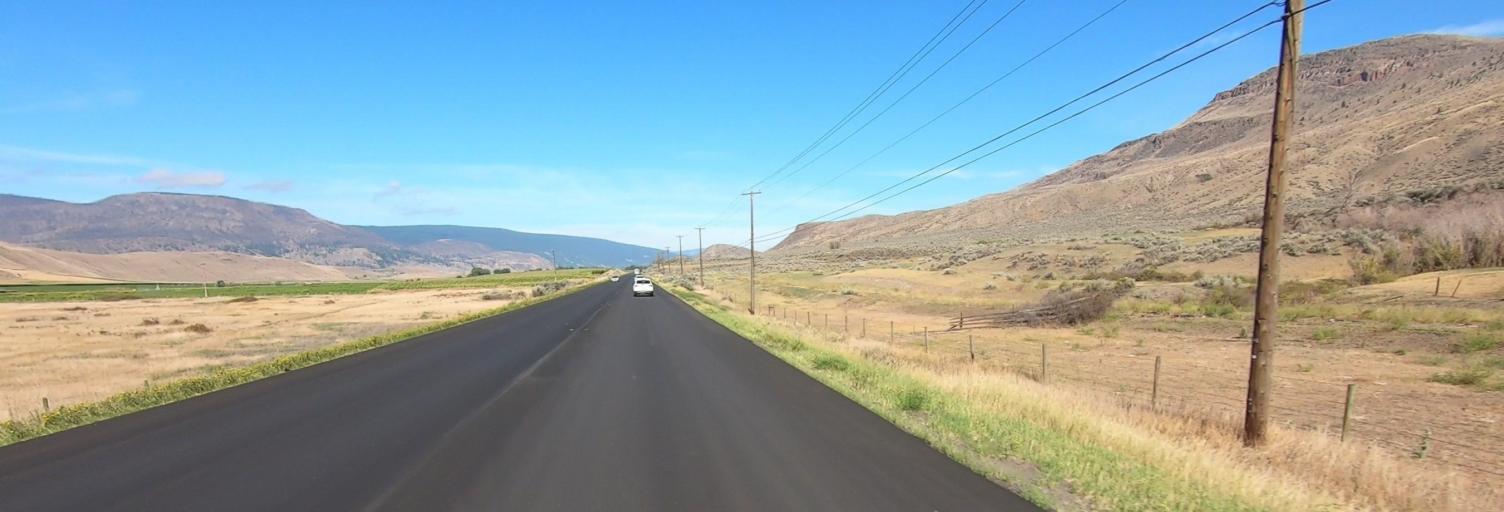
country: CA
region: British Columbia
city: Cache Creek
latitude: 50.7960
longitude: -121.2523
